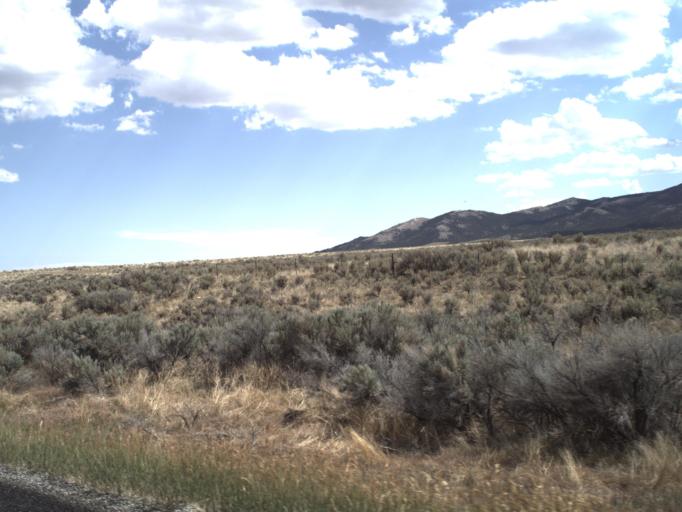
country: US
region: Idaho
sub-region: Minidoka County
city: Rupert
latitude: 41.9887
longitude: -113.1808
